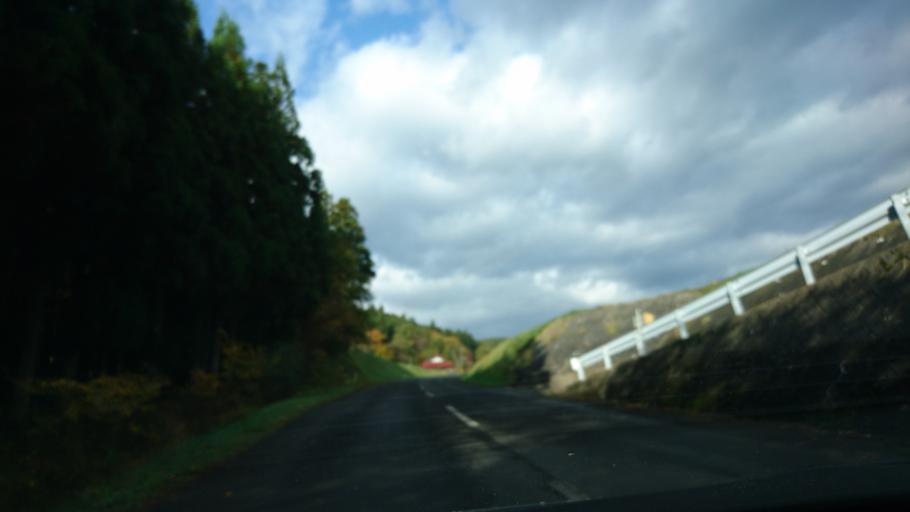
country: JP
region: Iwate
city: Mizusawa
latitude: 39.0879
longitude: 140.9812
